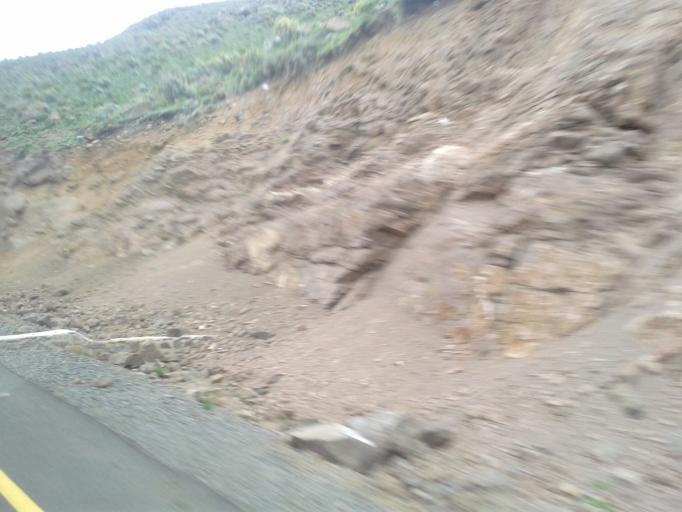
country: LS
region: Maseru
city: Nako
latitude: -29.7667
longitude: 28.0080
